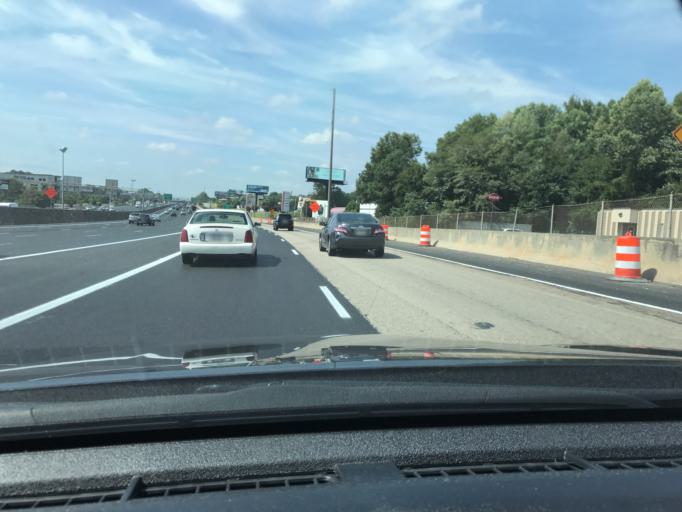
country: US
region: Georgia
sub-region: DeKalb County
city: Doraville
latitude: 33.8881
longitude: -84.2656
